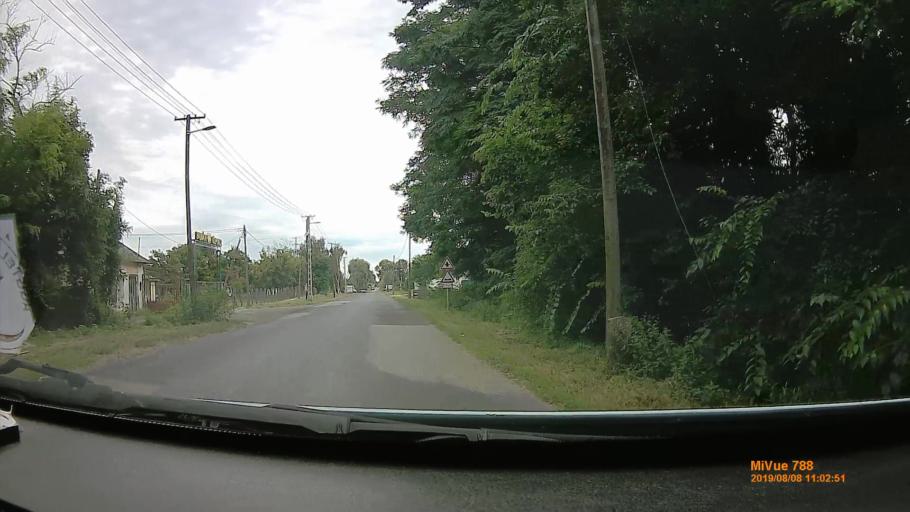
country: HU
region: Szabolcs-Szatmar-Bereg
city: Balkany
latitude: 47.7700
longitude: 21.8363
